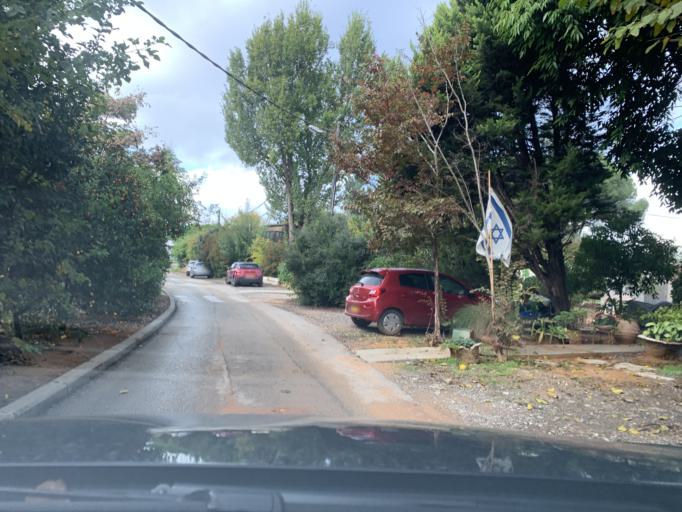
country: PS
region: West Bank
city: Qalqilyah
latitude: 32.1982
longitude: 34.9498
